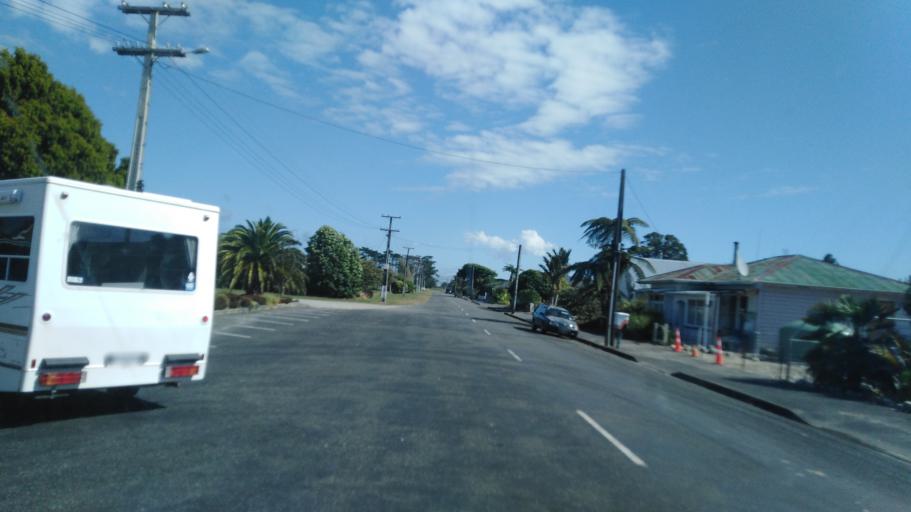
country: NZ
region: West Coast
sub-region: Buller District
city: Westport
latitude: -41.2479
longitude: 172.1114
